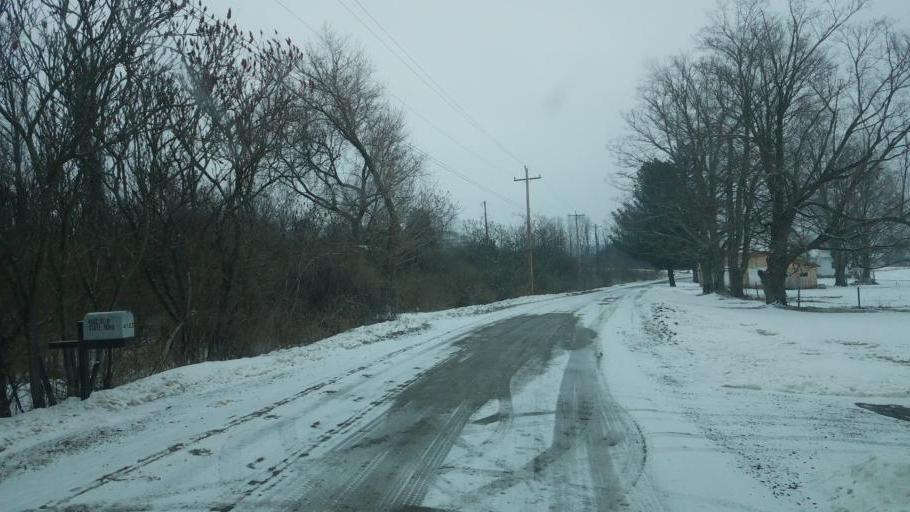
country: US
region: Pennsylvania
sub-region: Tioga County
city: Elkland
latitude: 42.1022
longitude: -77.4536
